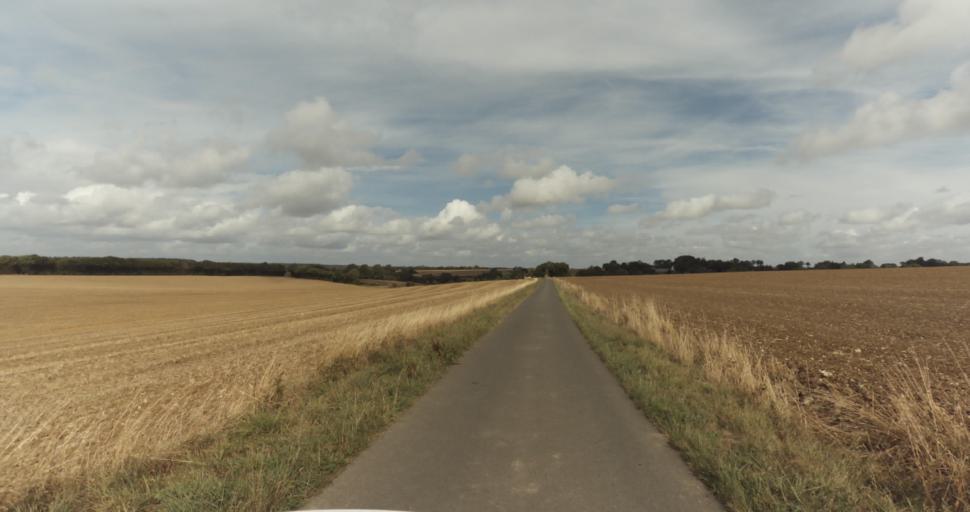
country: FR
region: Lower Normandy
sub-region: Departement de l'Orne
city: Gace
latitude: 48.8052
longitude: 0.3756
